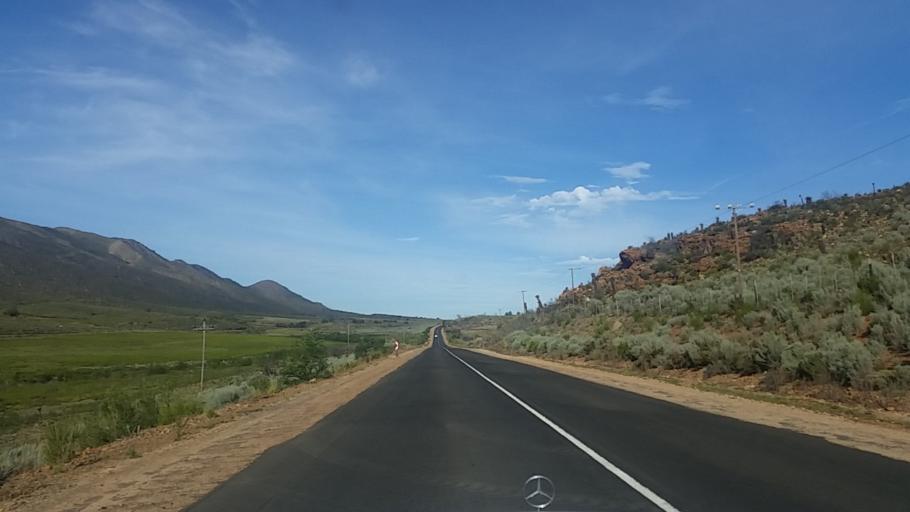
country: ZA
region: Western Cape
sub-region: Eden District Municipality
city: George
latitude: -33.8198
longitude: 22.3683
